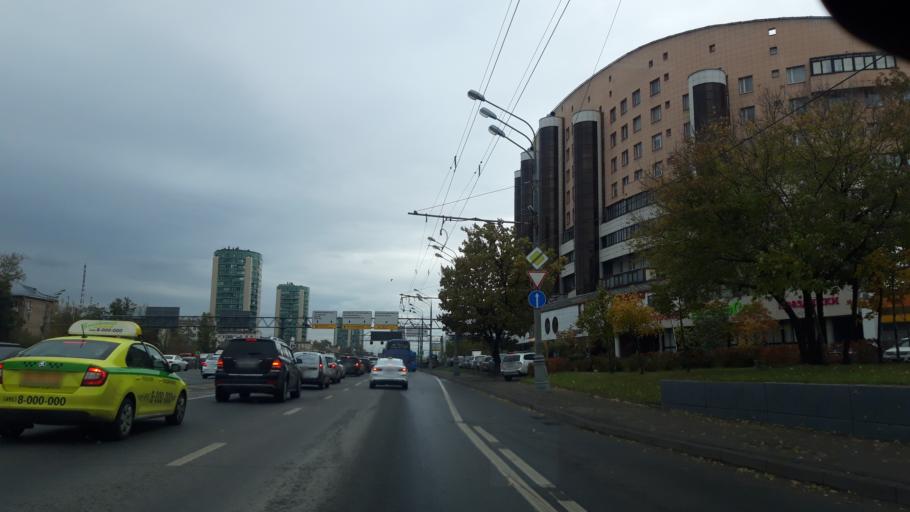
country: RU
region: Moskovskaya
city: Khoroshevo-Mnevniki
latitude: 55.7783
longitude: 37.4560
